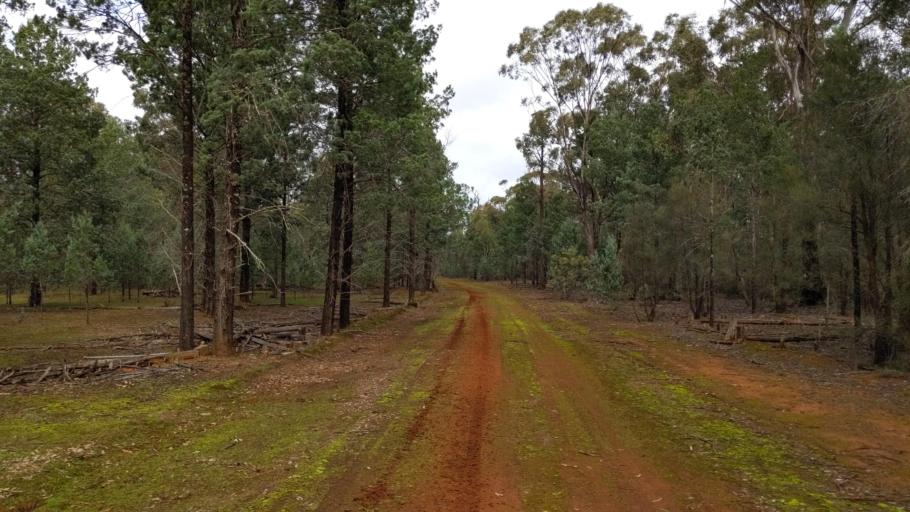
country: AU
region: New South Wales
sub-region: Coolamon
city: Coolamon
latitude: -34.8300
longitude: 146.9355
